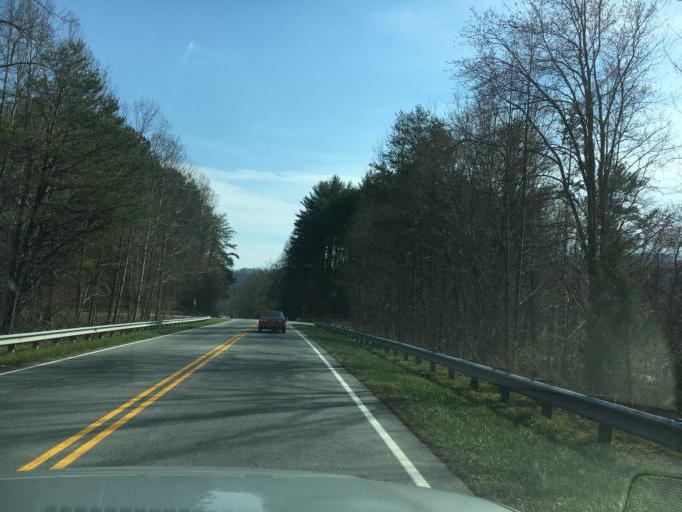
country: US
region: North Carolina
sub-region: McDowell County
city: West Marion
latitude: 35.5876
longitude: -81.9829
